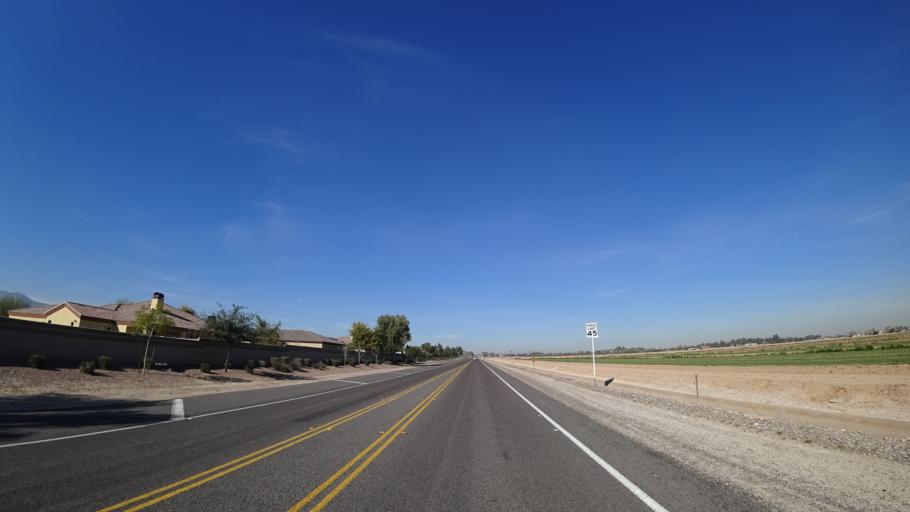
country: US
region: Arizona
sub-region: Maricopa County
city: Citrus Park
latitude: 33.5167
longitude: -112.4442
